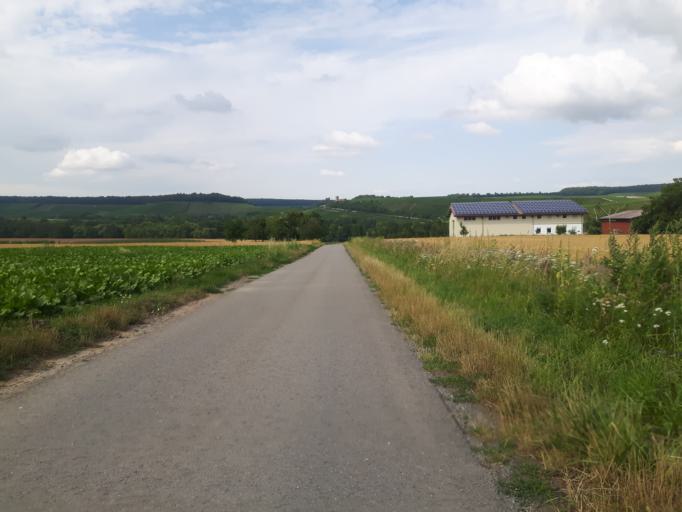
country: DE
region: Baden-Wuerttemberg
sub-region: Regierungsbezirk Stuttgart
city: Brackenheim
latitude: 49.0842
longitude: 9.0500
